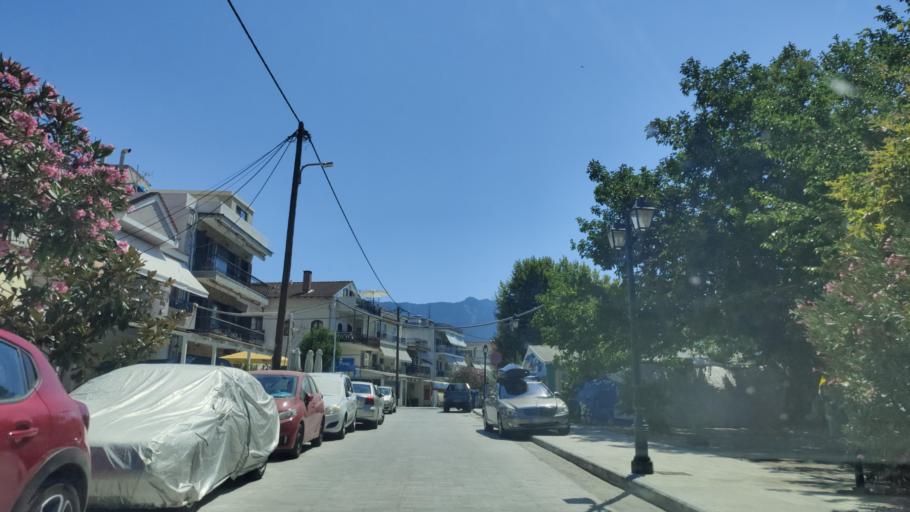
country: GR
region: East Macedonia and Thrace
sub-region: Nomos Kavalas
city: Thasos
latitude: 40.7831
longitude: 24.7152
